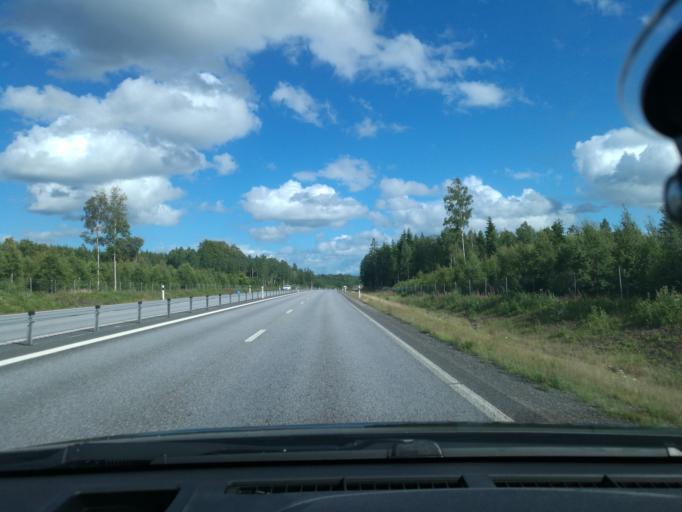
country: SE
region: Kronoberg
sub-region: Vaxjo Kommun
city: Gemla
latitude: 56.9060
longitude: 14.6565
